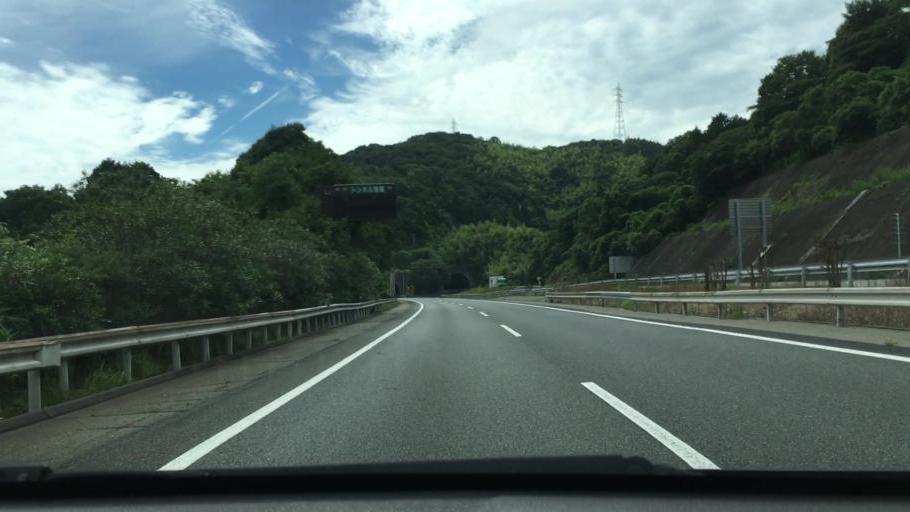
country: JP
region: Yamaguchi
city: Hofu
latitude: 34.0723
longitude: 131.6756
